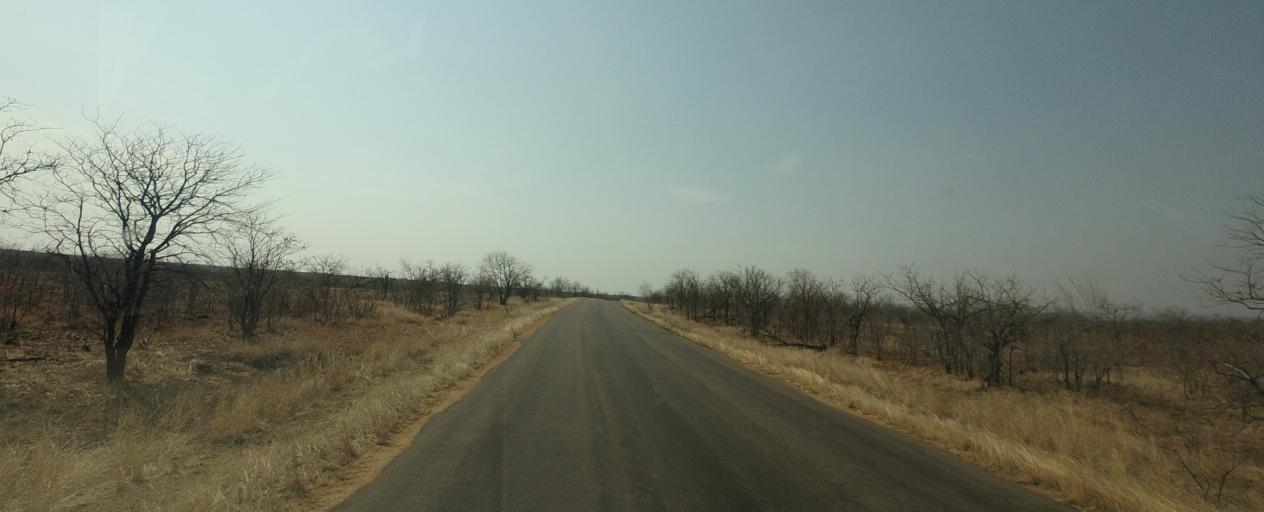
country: ZA
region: Limpopo
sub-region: Mopani District Municipality
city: Phalaborwa
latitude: -23.9408
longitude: 31.6124
